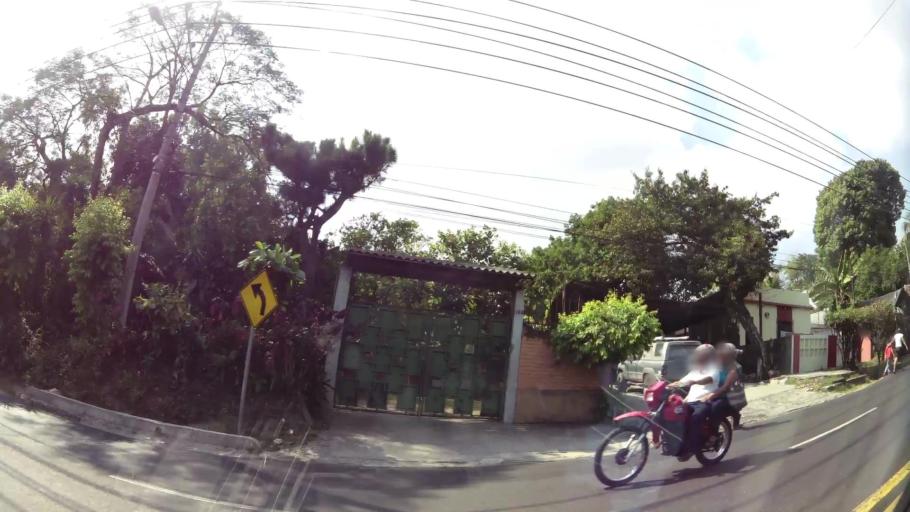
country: SV
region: San Salvador
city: Delgado
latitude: 13.7079
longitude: -89.1711
